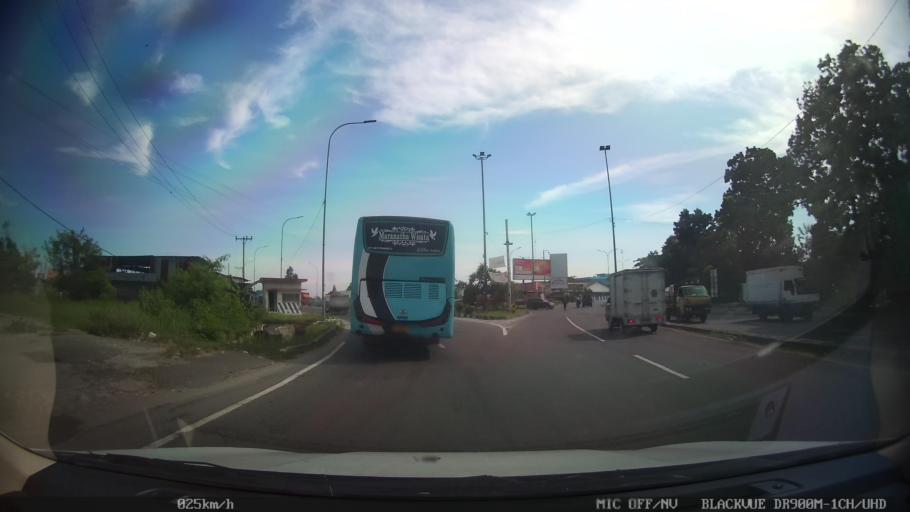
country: ID
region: North Sumatra
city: Sunggal
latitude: 3.6146
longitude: 98.6284
